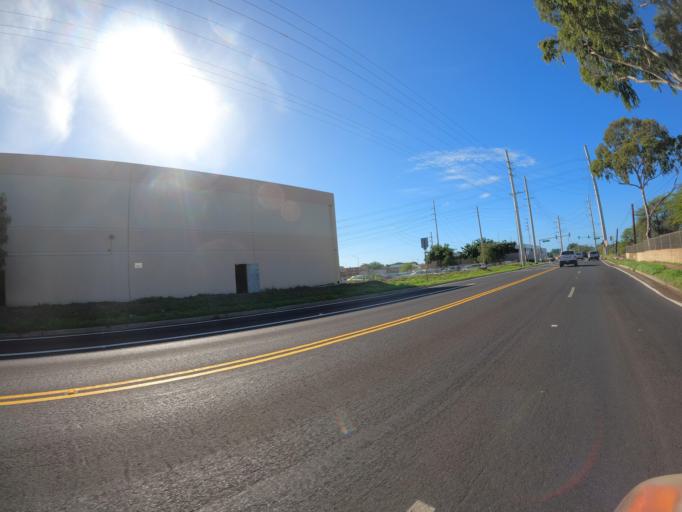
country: US
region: Hawaii
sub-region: Honolulu County
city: Halawa
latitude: 21.3560
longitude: -157.9304
